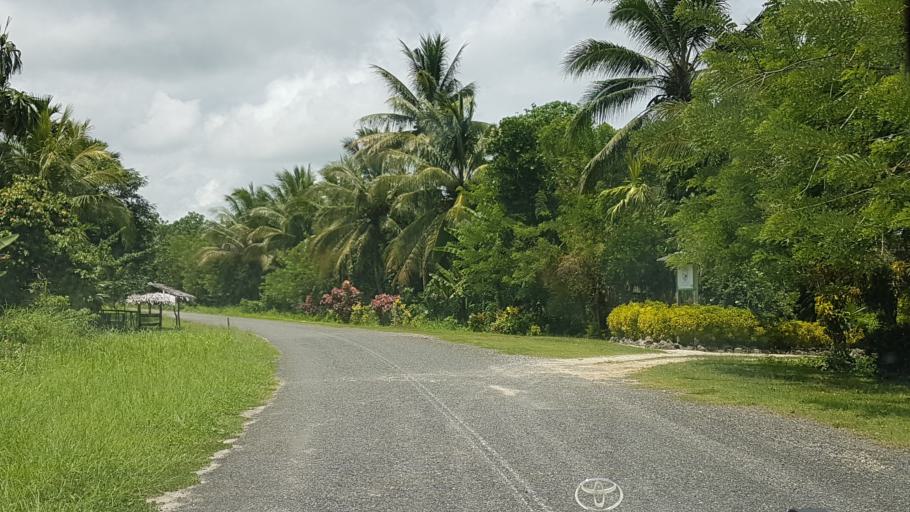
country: PG
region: Madang
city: Madang
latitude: -4.4931
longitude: 145.4289
